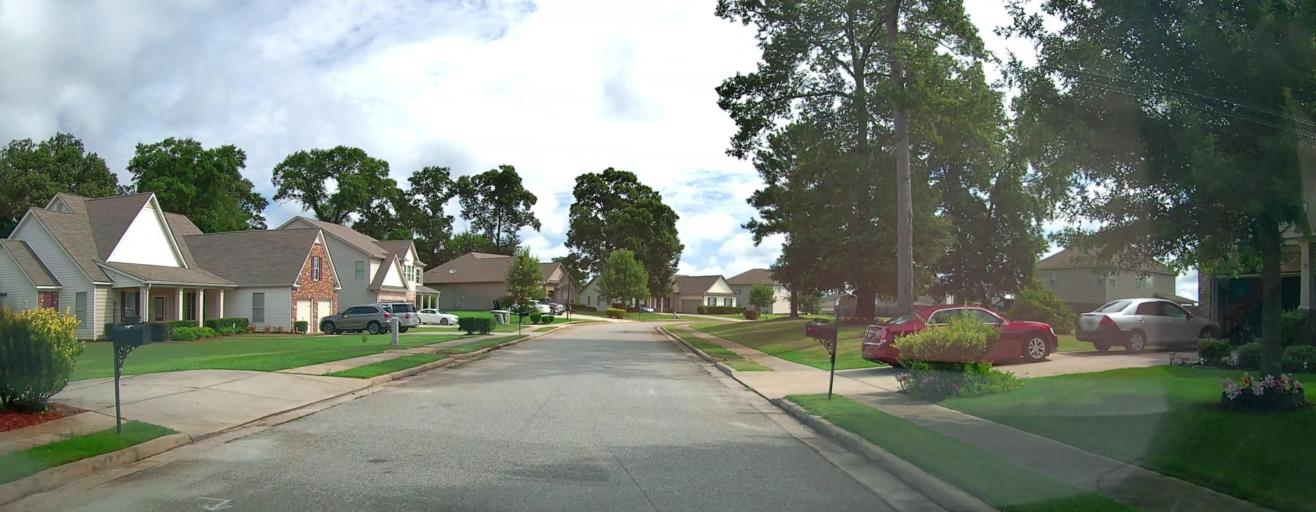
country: US
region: Georgia
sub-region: Peach County
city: Byron
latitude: 32.6286
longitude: -83.7385
